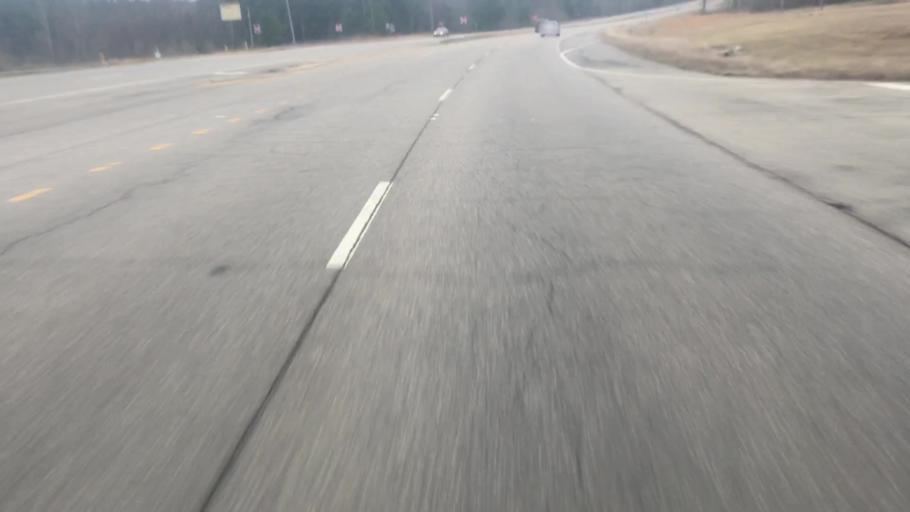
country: US
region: Alabama
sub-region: Walker County
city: Cordova
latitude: 33.8200
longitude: -87.1535
